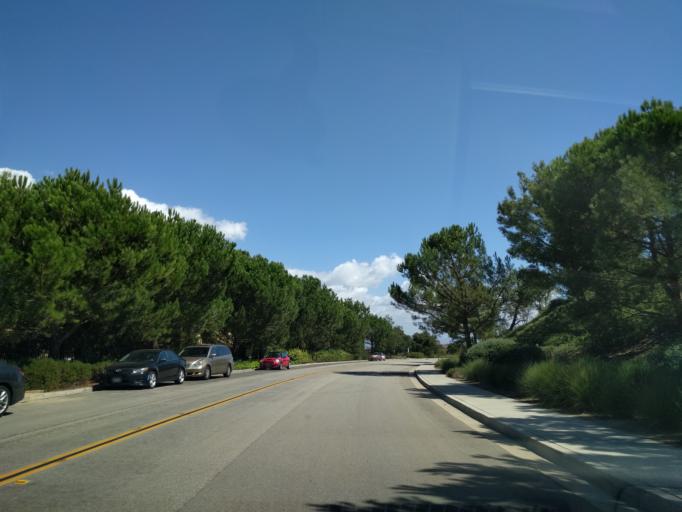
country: US
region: California
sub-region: Orange County
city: San Joaquin Hills
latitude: 33.6064
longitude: -117.8063
